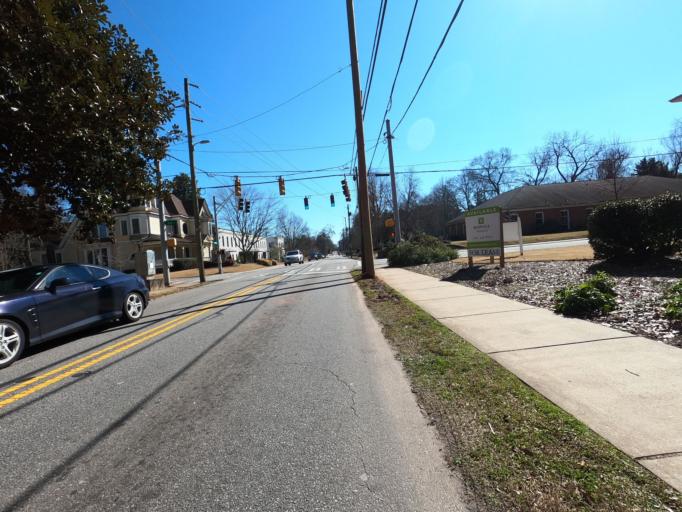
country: US
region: Georgia
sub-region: Clarke County
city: Athens
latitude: 33.9596
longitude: -83.3900
